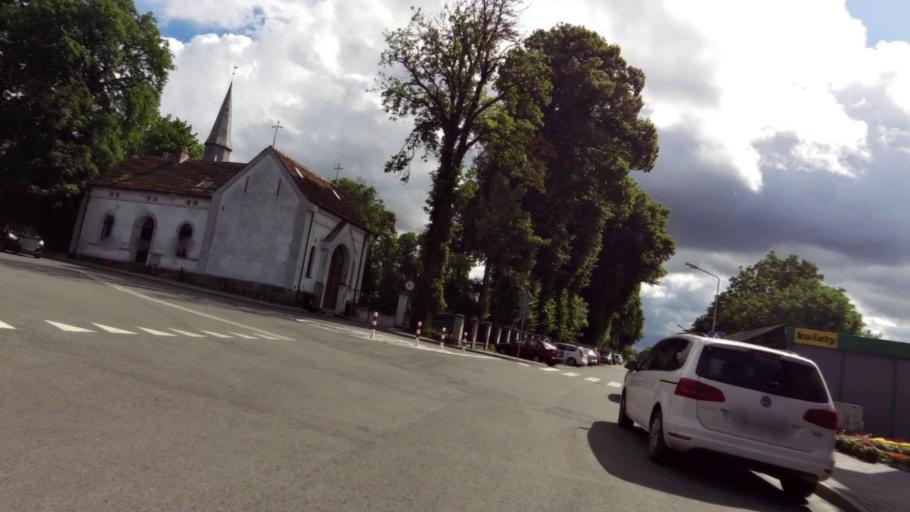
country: PL
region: West Pomeranian Voivodeship
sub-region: Powiat slawienski
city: Darlowo
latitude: 54.4240
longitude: 16.4146
